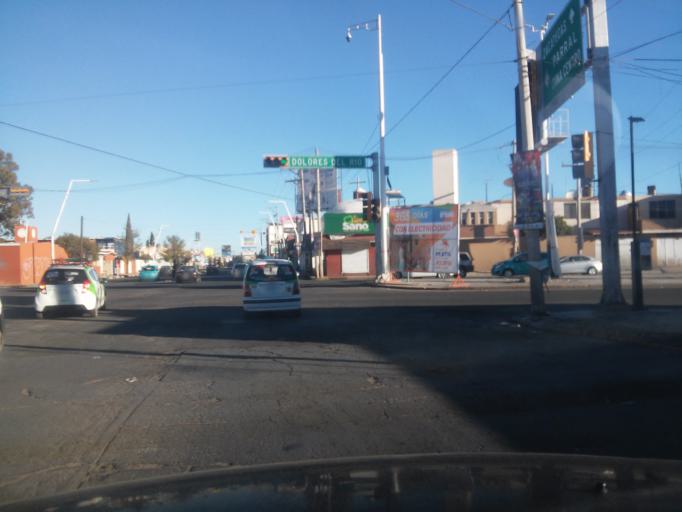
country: MX
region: Durango
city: Victoria de Durango
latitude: 24.0171
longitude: -104.6517
